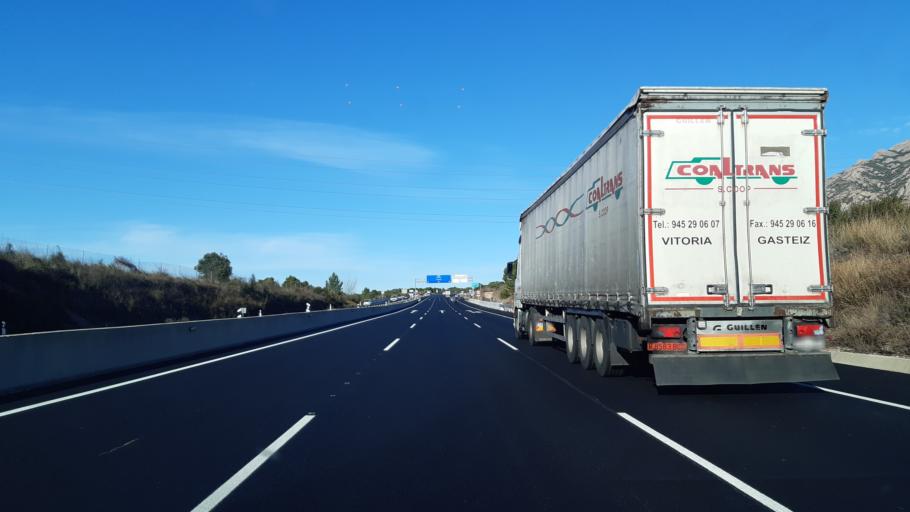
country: ES
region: Catalonia
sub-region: Provincia de Barcelona
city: Collbato
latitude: 41.5530
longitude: 1.8418
